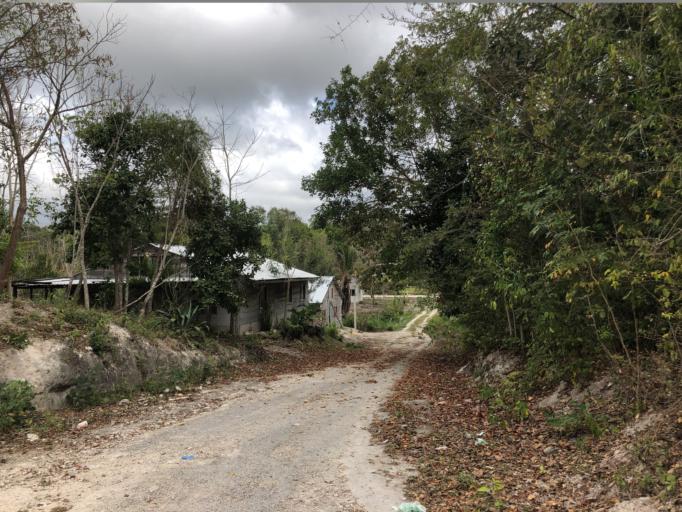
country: MX
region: Quintana Roo
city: Nicolas Bravo
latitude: 18.4504
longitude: -89.3084
